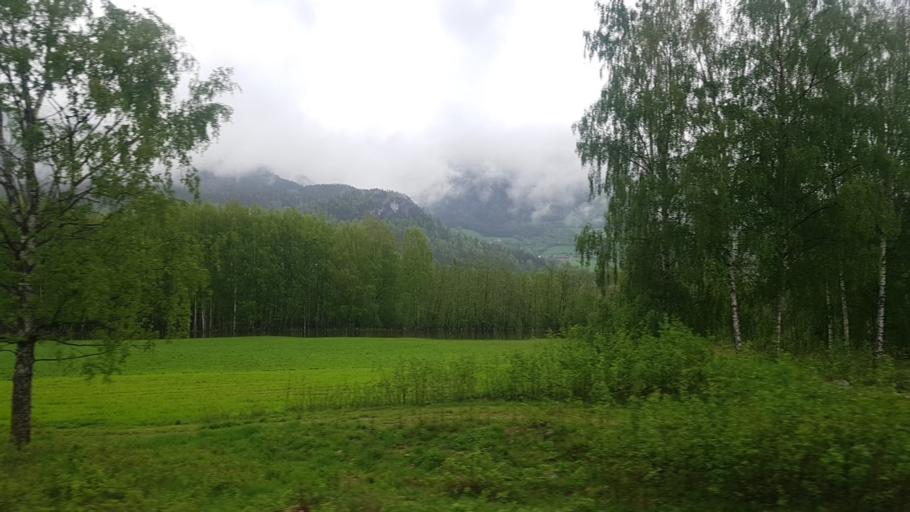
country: NO
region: Oppland
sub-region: Ringebu
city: Ringebu
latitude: 61.4639
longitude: 10.1909
